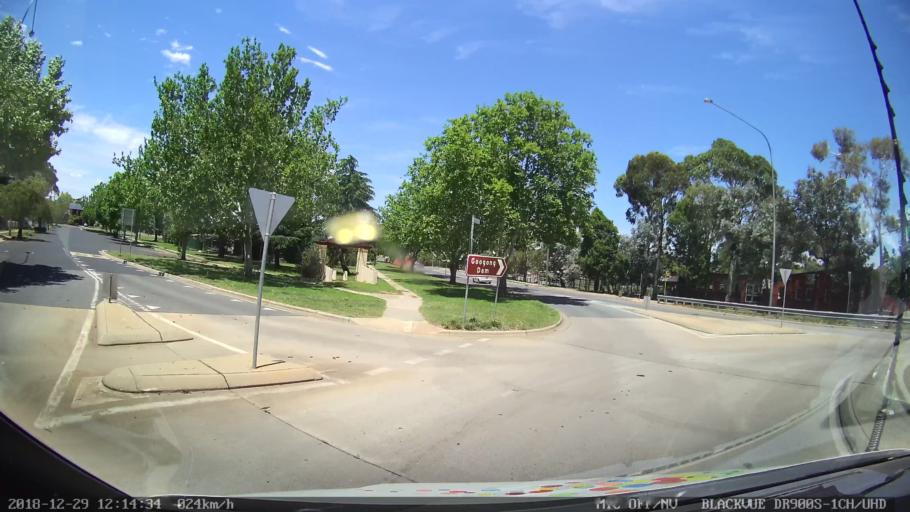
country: AU
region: New South Wales
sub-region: Queanbeyan
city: Queanbeyan
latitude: -35.3562
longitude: 149.2331
